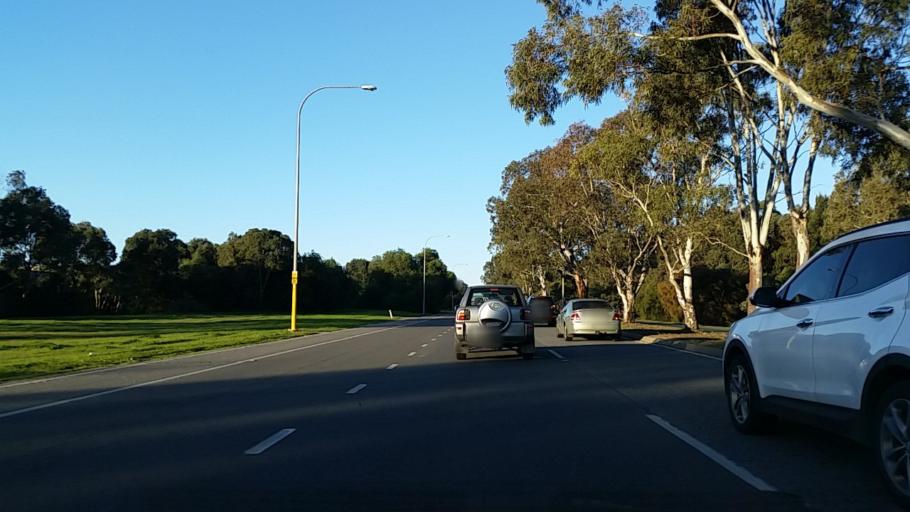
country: AU
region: South Australia
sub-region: Port Adelaide Enfield
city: Enfield
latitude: -34.8260
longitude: 138.6070
